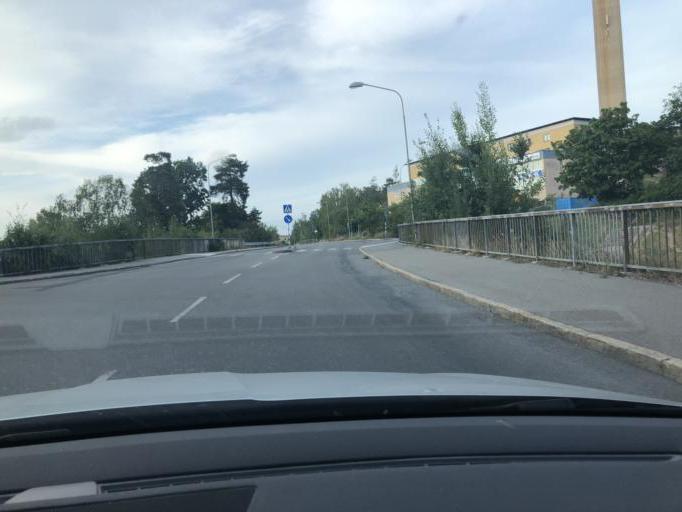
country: SE
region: Stockholm
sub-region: Botkyrka Kommun
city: Fittja
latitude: 59.2779
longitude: 17.8867
